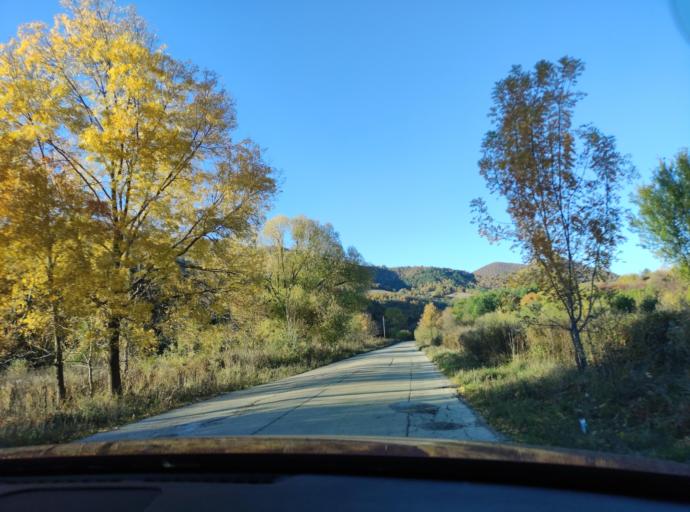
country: BG
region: Montana
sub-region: Obshtina Chiprovtsi
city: Chiprovtsi
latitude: 43.3883
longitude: 22.9223
